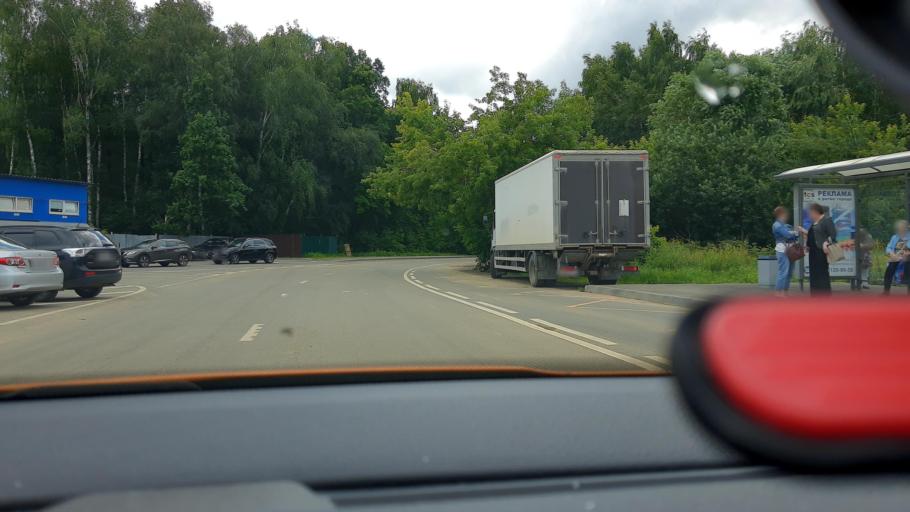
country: RU
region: Moskovskaya
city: Krasnogorsk
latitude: 55.8703
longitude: 37.3462
